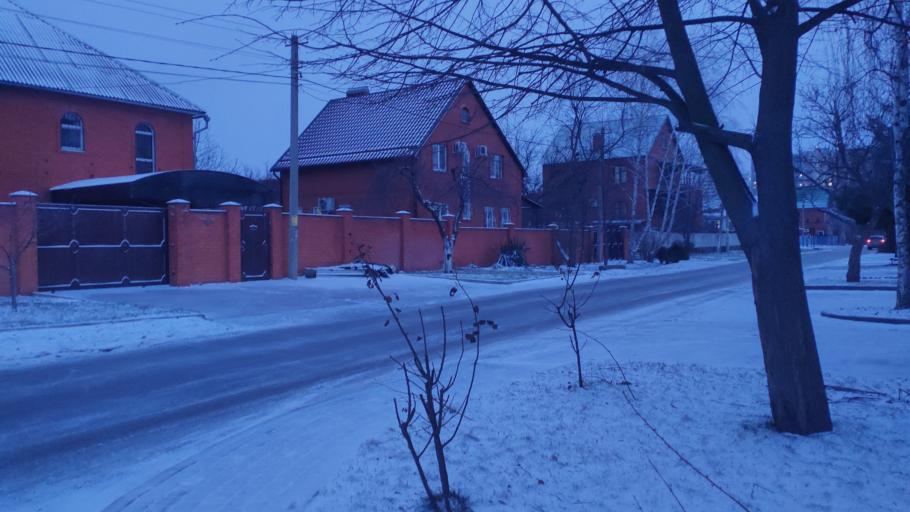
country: RU
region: Krasnodarskiy
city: Krasnodar
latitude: 45.0759
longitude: 39.0121
